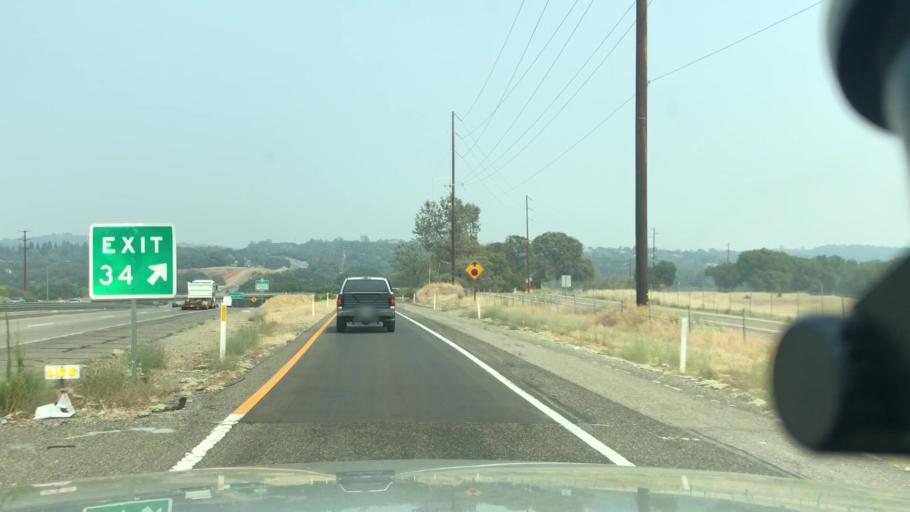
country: US
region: California
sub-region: El Dorado County
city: Cameron Park
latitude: 38.6559
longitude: -121.0024
